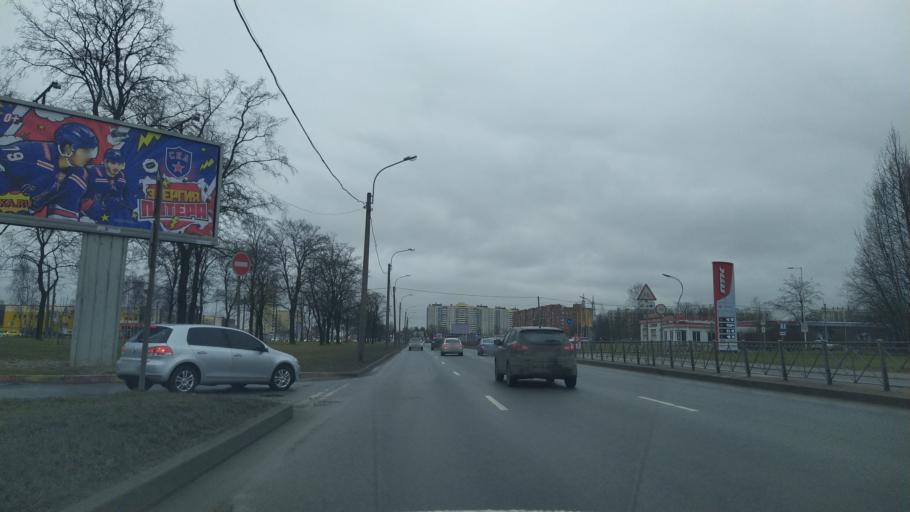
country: RU
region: St.-Petersburg
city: Grazhdanka
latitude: 60.0200
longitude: 30.4318
